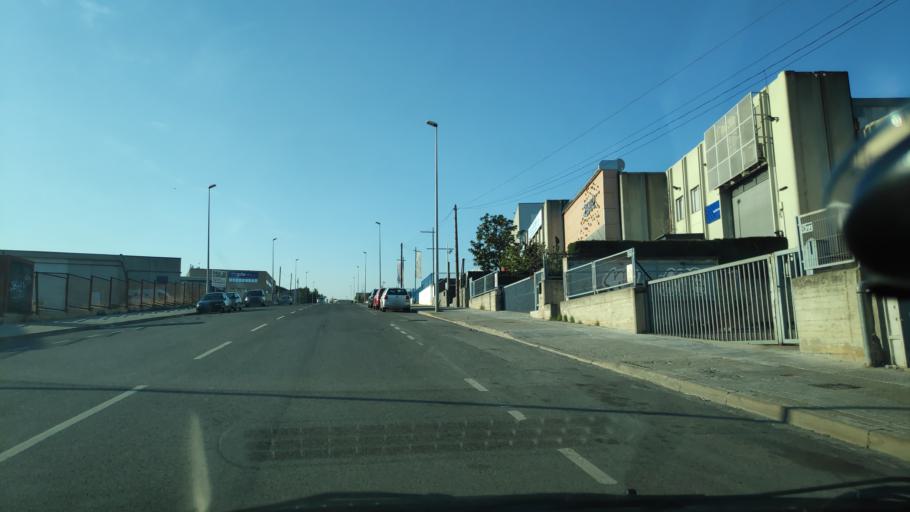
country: ES
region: Catalonia
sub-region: Provincia de Barcelona
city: Terrassa
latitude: 41.5371
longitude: 2.0318
